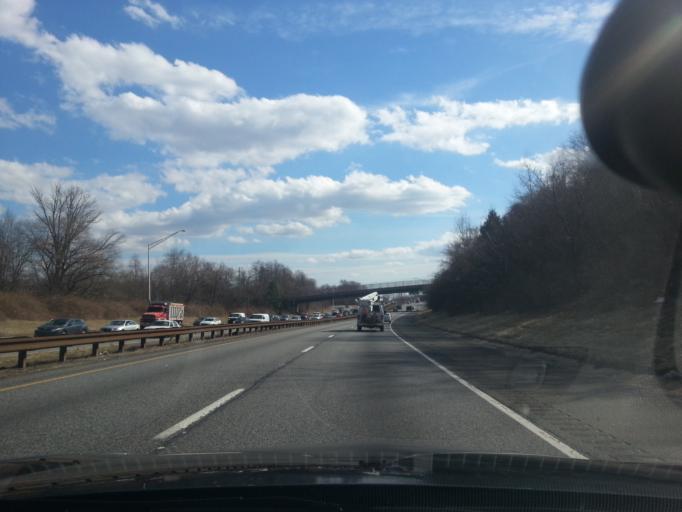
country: US
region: Pennsylvania
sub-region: Delaware County
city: Woodlyn
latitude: 39.8805
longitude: -75.3517
